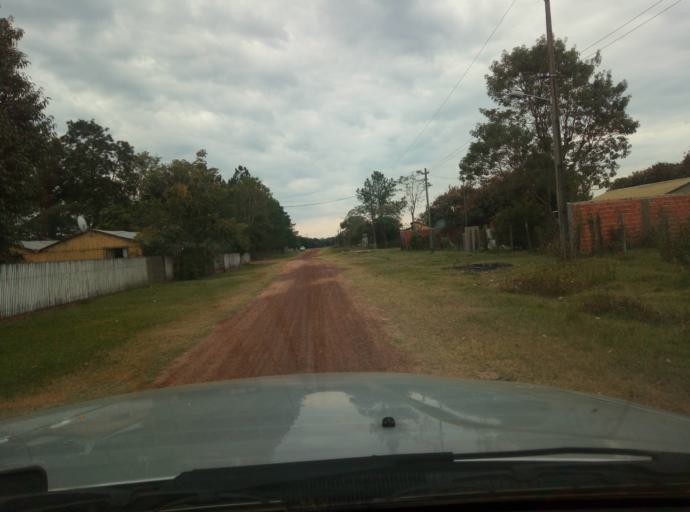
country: PY
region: Caaguazu
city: Carayao
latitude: -25.1533
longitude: -56.3337
